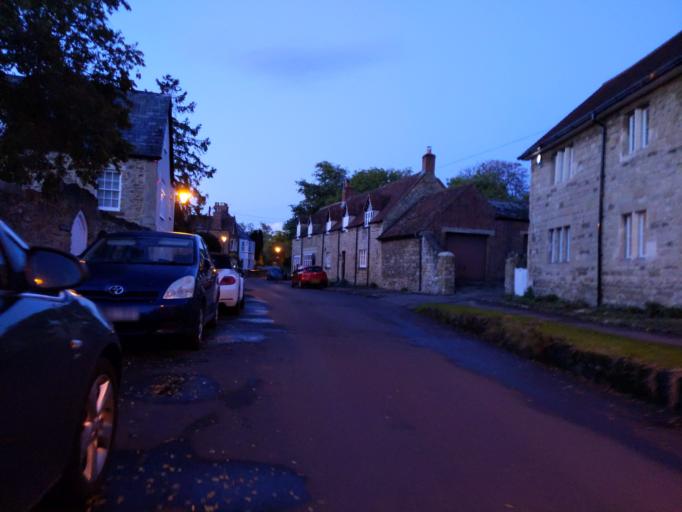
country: GB
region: England
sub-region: Oxfordshire
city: Oxford
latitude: 51.7296
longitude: -1.2378
